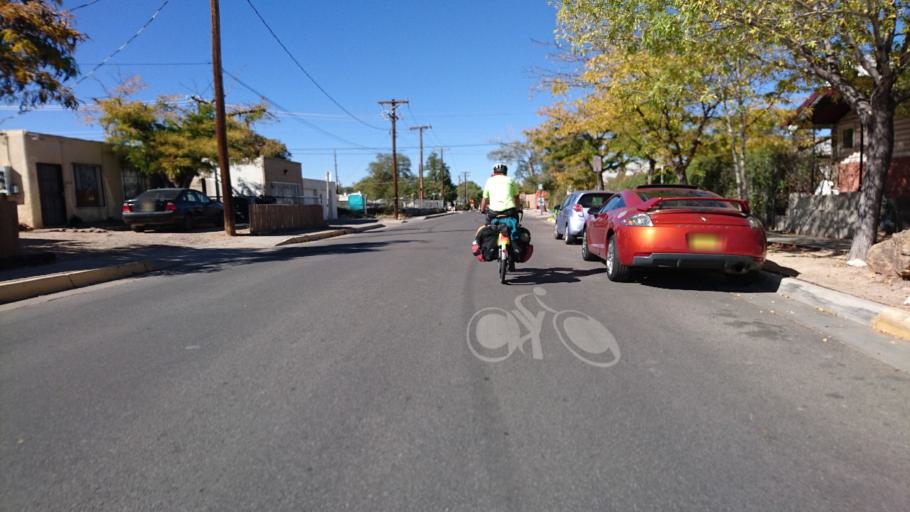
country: US
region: New Mexico
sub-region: Bernalillo County
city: Albuquerque
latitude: 35.0792
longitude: -106.6185
